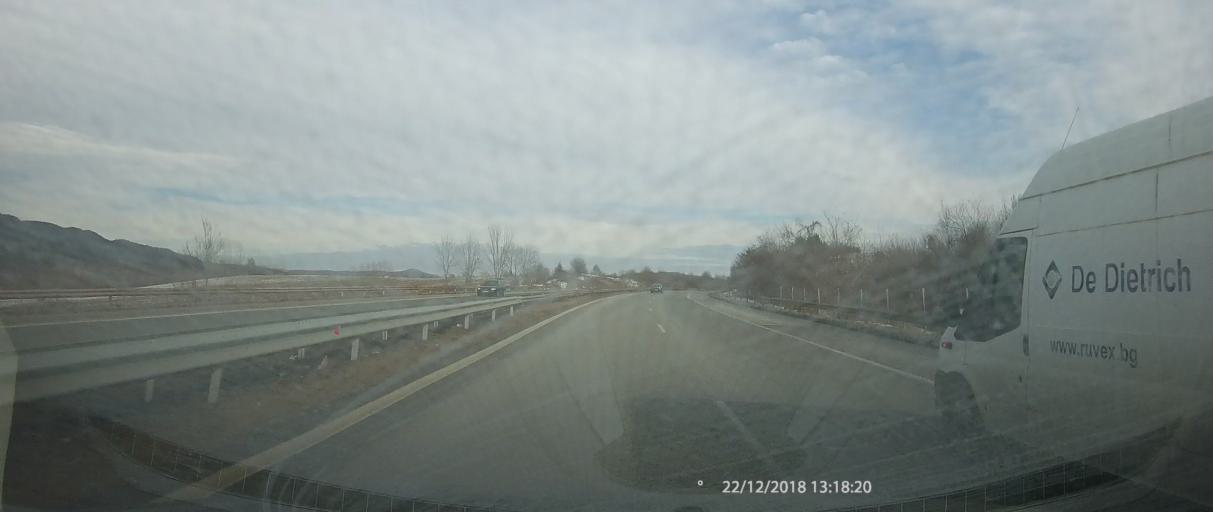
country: BG
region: Sofiya
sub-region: Obshtina Pravets
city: Pravets
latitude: 42.9402
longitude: 23.9738
